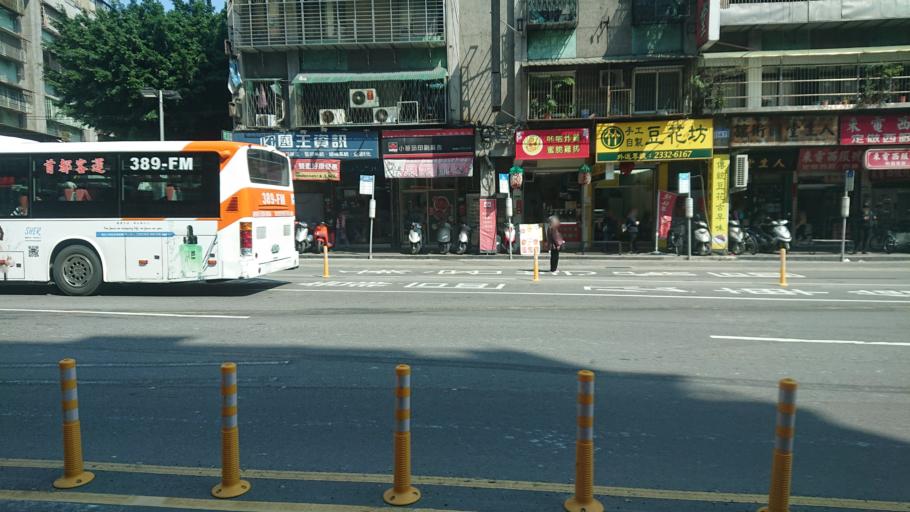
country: TW
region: Taipei
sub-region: Taipei
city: Banqiao
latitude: 25.0287
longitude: 121.5004
